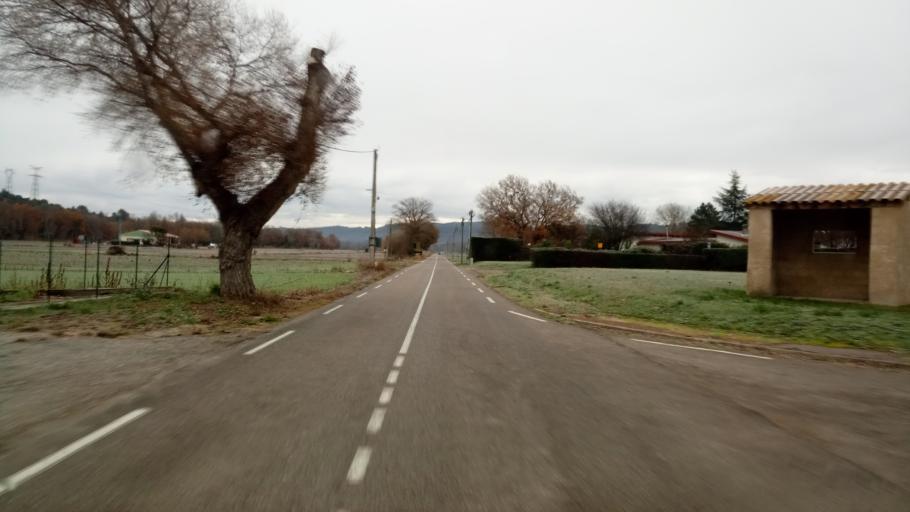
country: FR
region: Provence-Alpes-Cote d'Azur
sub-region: Departement du Var
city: Vinon-sur-Verdon
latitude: 43.7278
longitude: 5.8265
